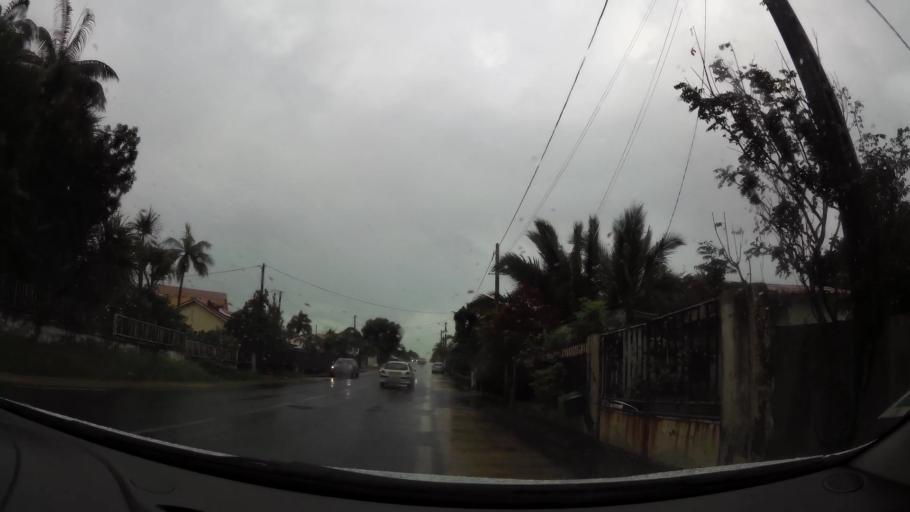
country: RE
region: Reunion
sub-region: Reunion
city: Saint-Benoit
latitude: -21.0201
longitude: 55.7027
